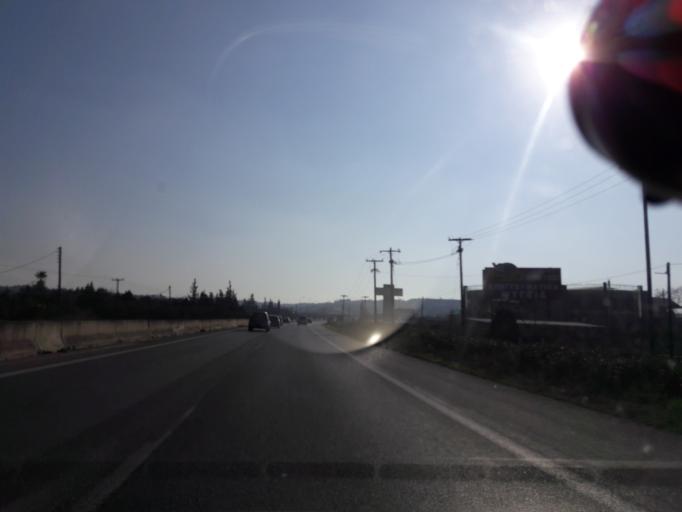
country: GR
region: Central Macedonia
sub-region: Nomos Thessalonikis
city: Neo Rysi
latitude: 40.5016
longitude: 23.0051
